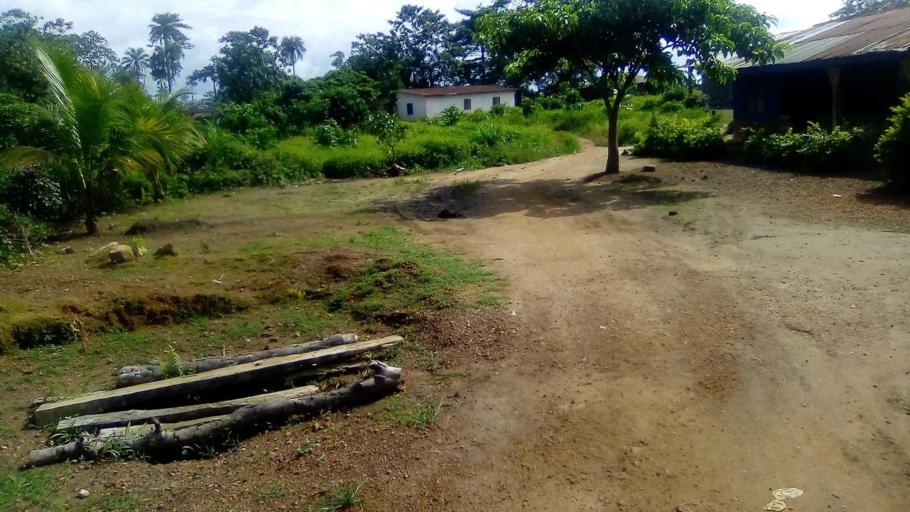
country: SL
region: Southern Province
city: Pujehun
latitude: 7.3632
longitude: -11.7293
